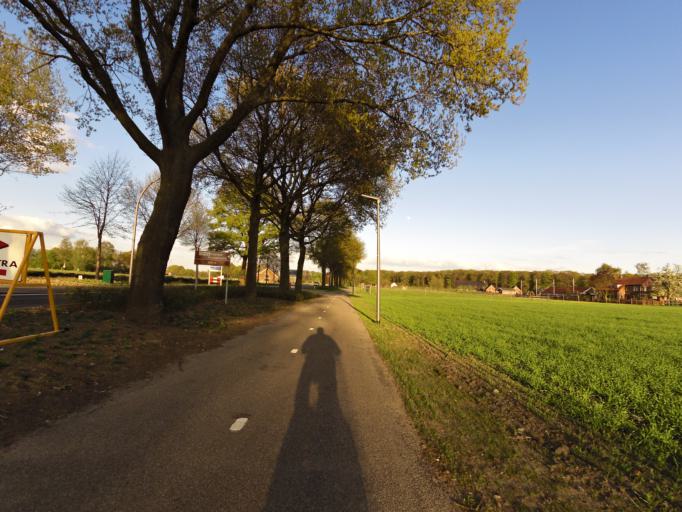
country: NL
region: Gelderland
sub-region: Oude IJsselstreek
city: Wisch
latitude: 51.9510
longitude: 6.4178
